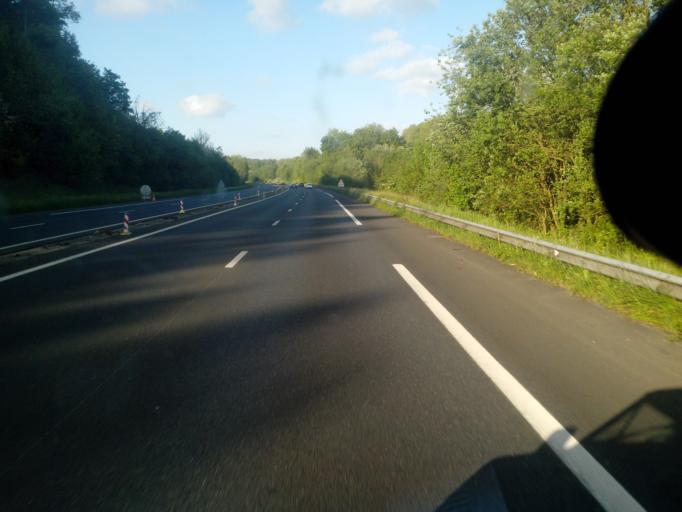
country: FR
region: Haute-Normandie
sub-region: Departement de la Seine-Maritime
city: Saint-Saens
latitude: 49.6602
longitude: 1.2992
